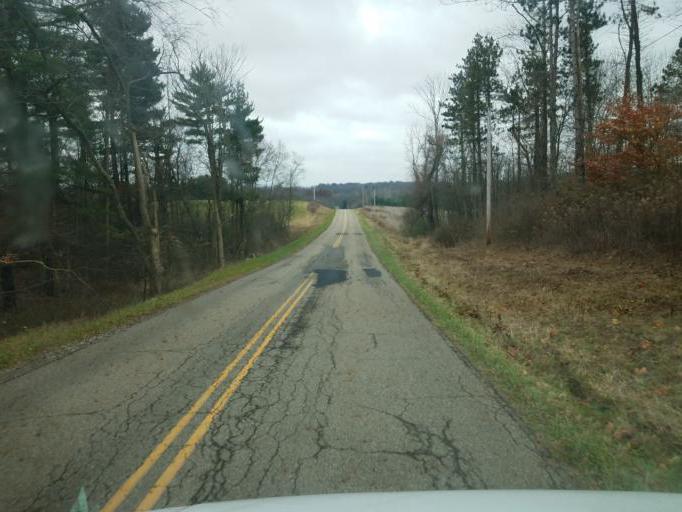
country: US
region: Ohio
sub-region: Knox County
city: Centerburg
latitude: 40.3565
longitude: -82.6256
